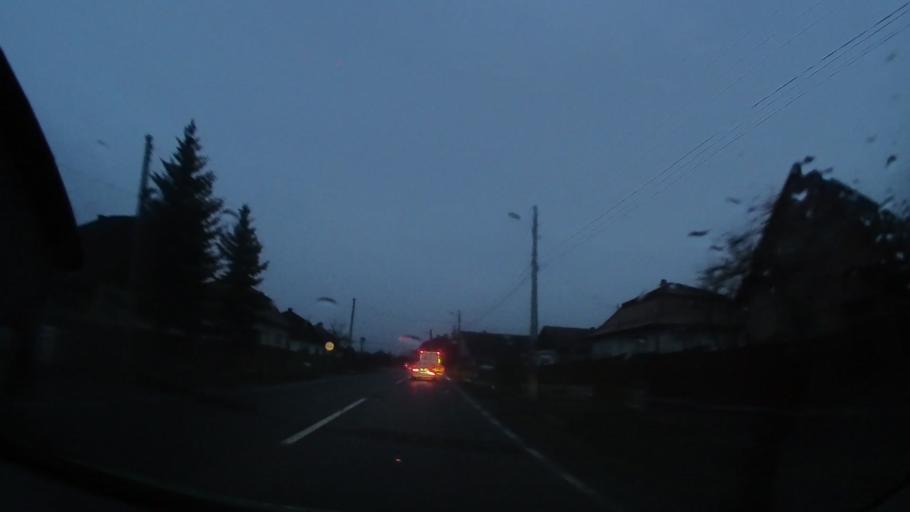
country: RO
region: Harghita
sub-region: Comuna Ditrau
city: Ditrau
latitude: 46.8118
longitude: 25.4940
